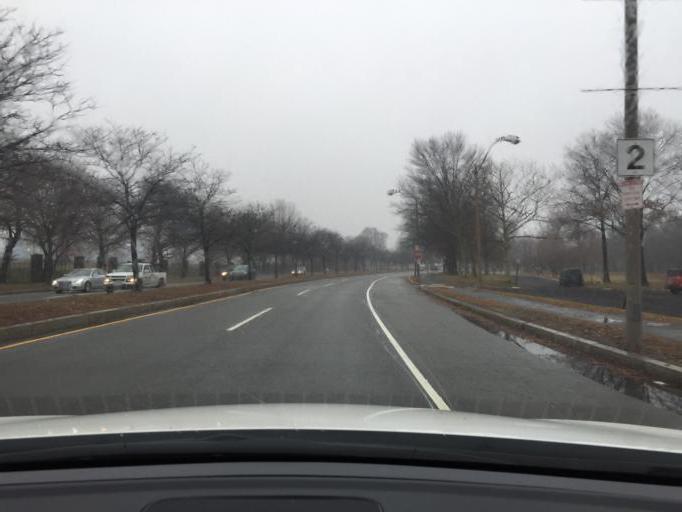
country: US
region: Massachusetts
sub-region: Middlesex County
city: Cambridge
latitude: 42.3687
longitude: -71.1308
